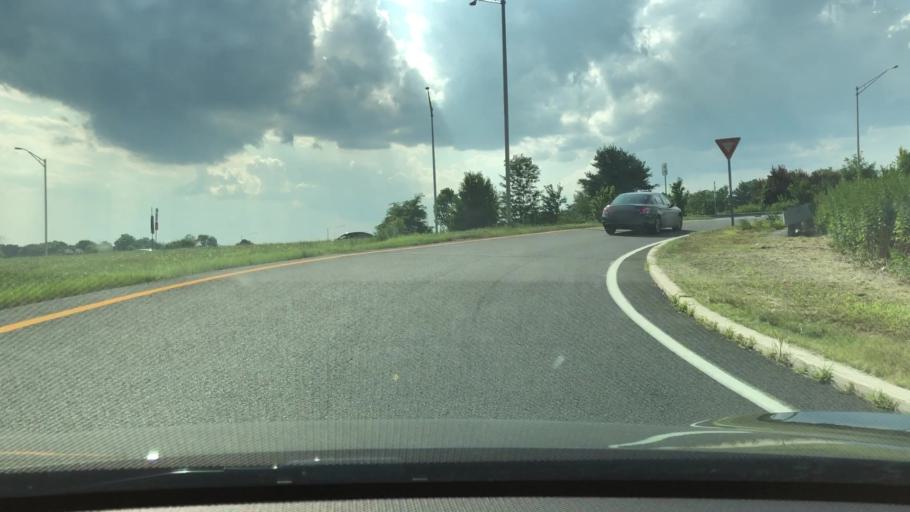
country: US
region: New Jersey
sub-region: Mercer County
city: Ewing
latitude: 40.2884
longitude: -74.8107
